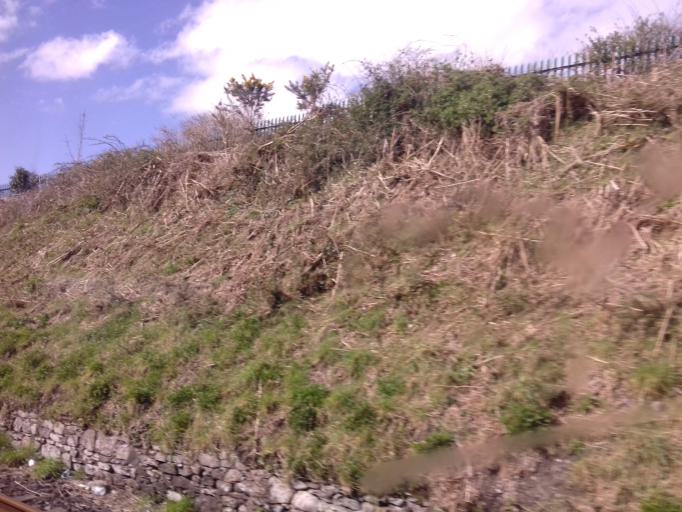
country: IE
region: Munster
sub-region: Ciarrai
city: Cill Airne
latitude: 52.0585
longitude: -9.4903
